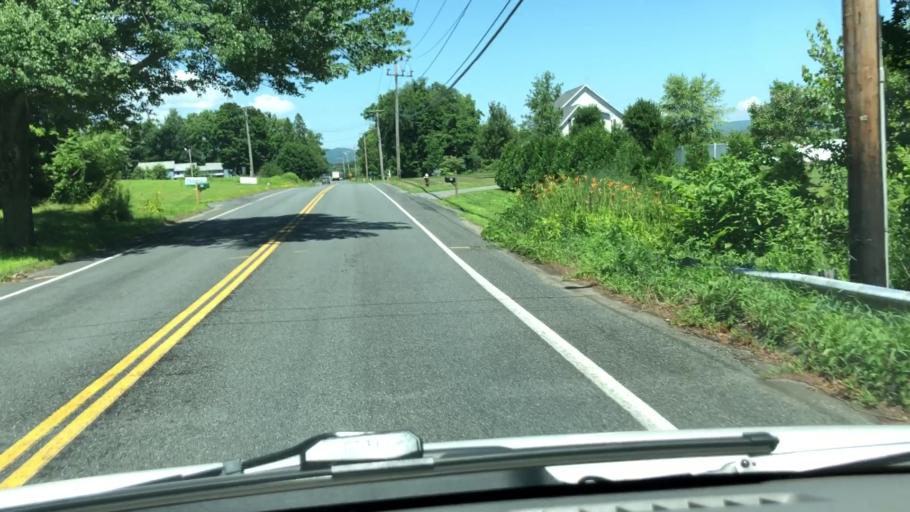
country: US
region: Massachusetts
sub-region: Hampshire County
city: Amherst Center
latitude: 42.3737
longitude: -72.5490
